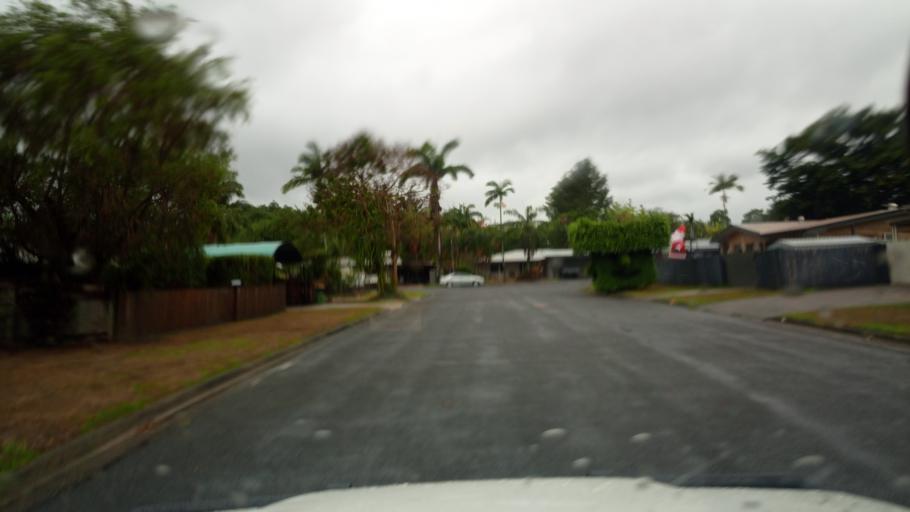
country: AU
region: Queensland
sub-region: Cairns
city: Woree
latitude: -16.9403
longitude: 145.7334
